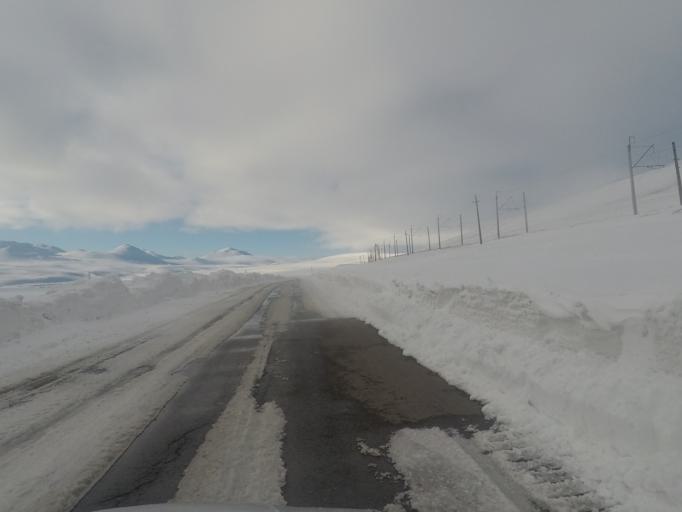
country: GE
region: Kvemo Kartli
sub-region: Tsalka
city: Tsalka
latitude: 41.4695
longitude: 43.8560
